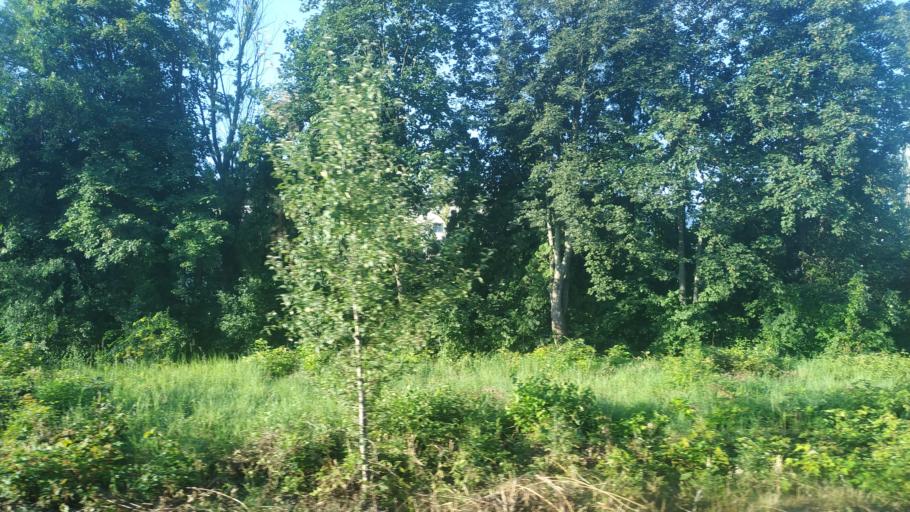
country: RO
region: Brasov
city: Brasov
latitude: 45.6610
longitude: 25.6180
